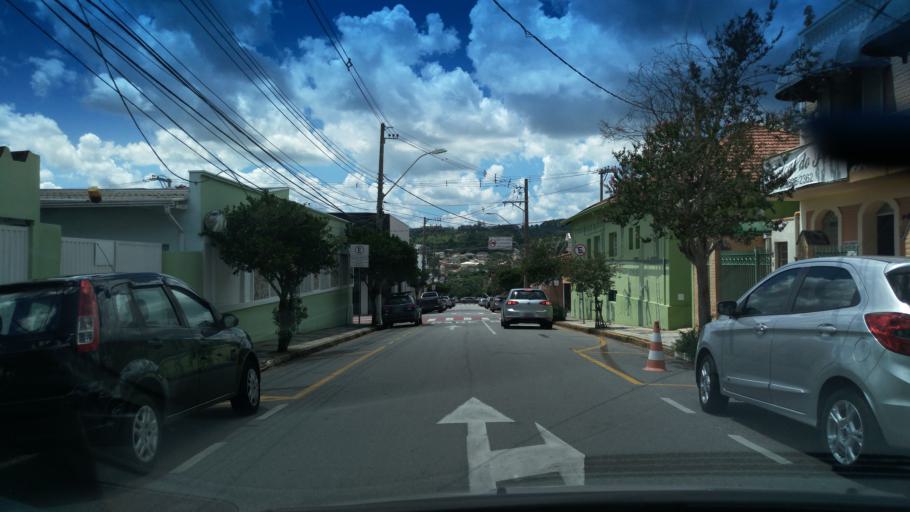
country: BR
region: Sao Paulo
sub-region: Vinhedo
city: Vinhedo
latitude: -23.0309
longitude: -46.9747
